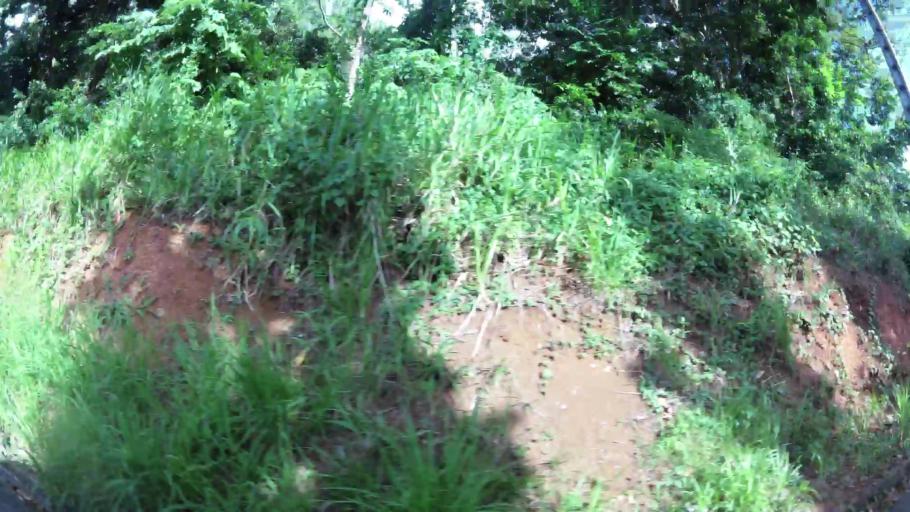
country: MQ
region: Martinique
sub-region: Martinique
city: Ducos
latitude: 14.5645
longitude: -60.9650
